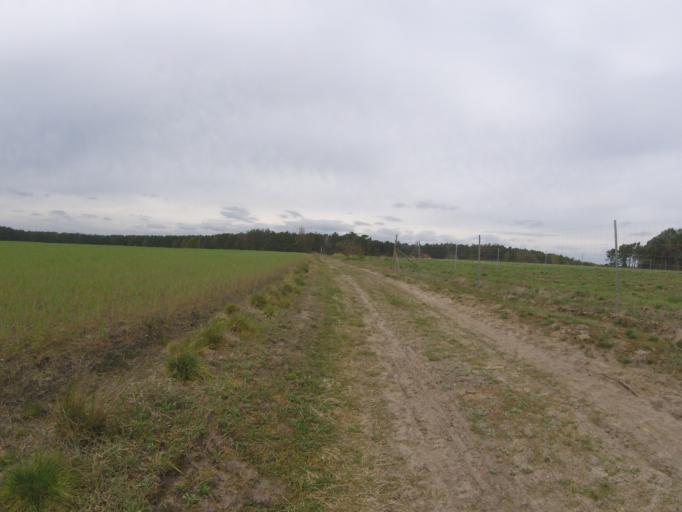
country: DE
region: Brandenburg
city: Bestensee
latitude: 52.2194
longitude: 13.6746
